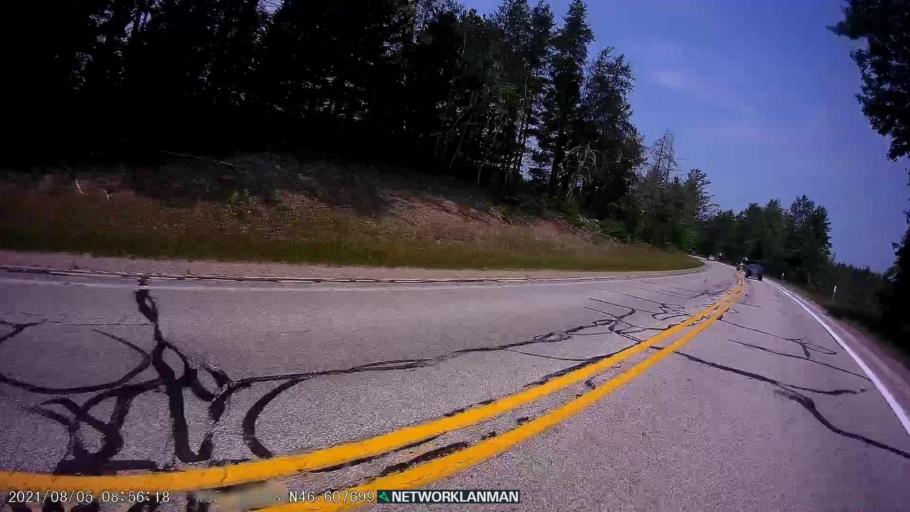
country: US
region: Michigan
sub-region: Luce County
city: Newberry
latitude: 46.6077
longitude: -85.1829
